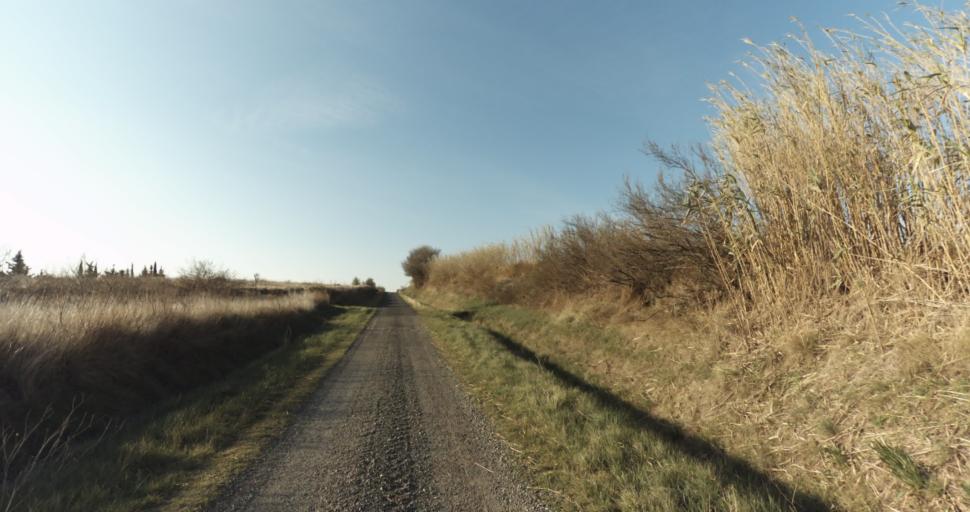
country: FR
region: Languedoc-Roussillon
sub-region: Departement de l'Herault
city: Marseillan
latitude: 43.3782
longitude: 3.5335
